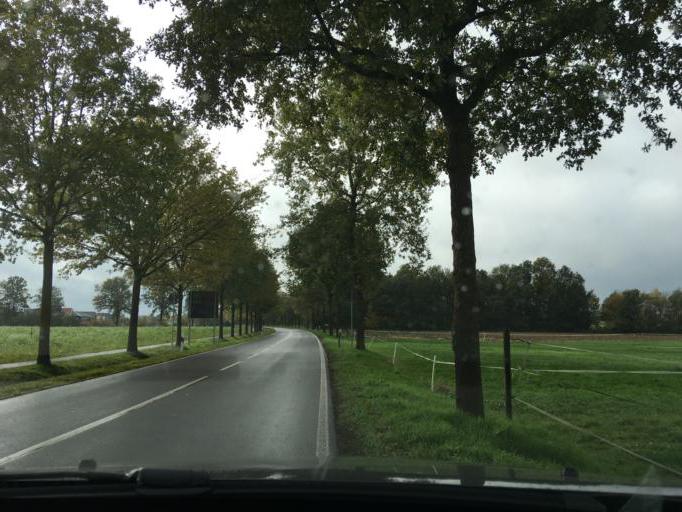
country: DE
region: North Rhine-Westphalia
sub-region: Regierungsbezirk Munster
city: Vreden
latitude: 52.0479
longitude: 6.8072
